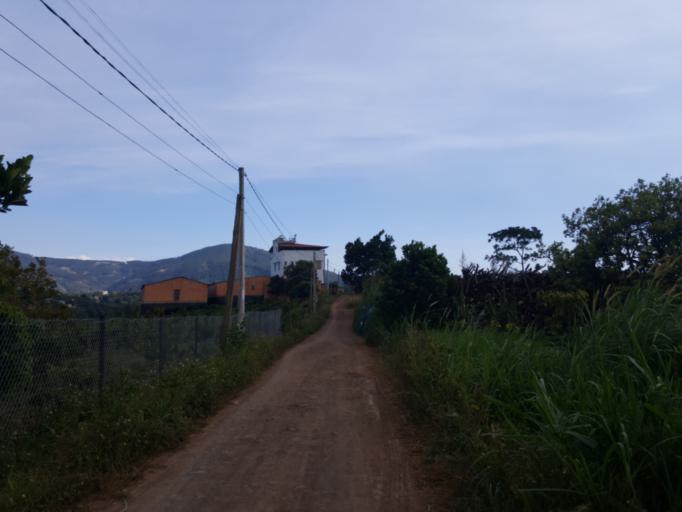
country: VN
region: Lam Dong
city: Duc Trong
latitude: 11.8390
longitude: 108.3475
